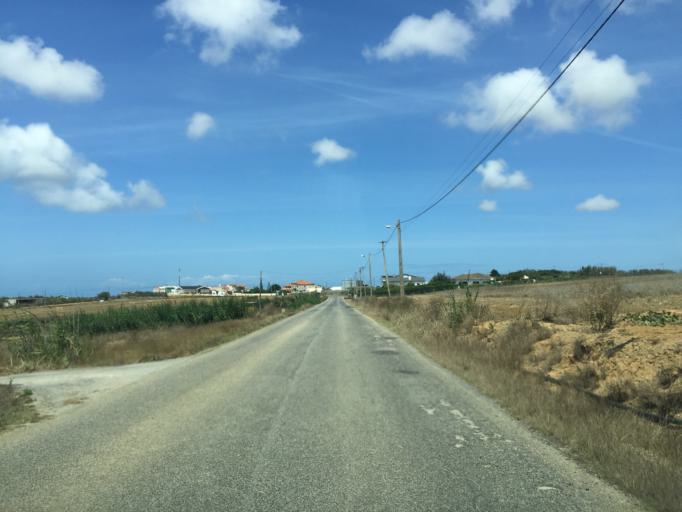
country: PT
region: Leiria
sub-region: Peniche
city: Atouguia da Baleia
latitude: 39.2897
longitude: -9.3070
